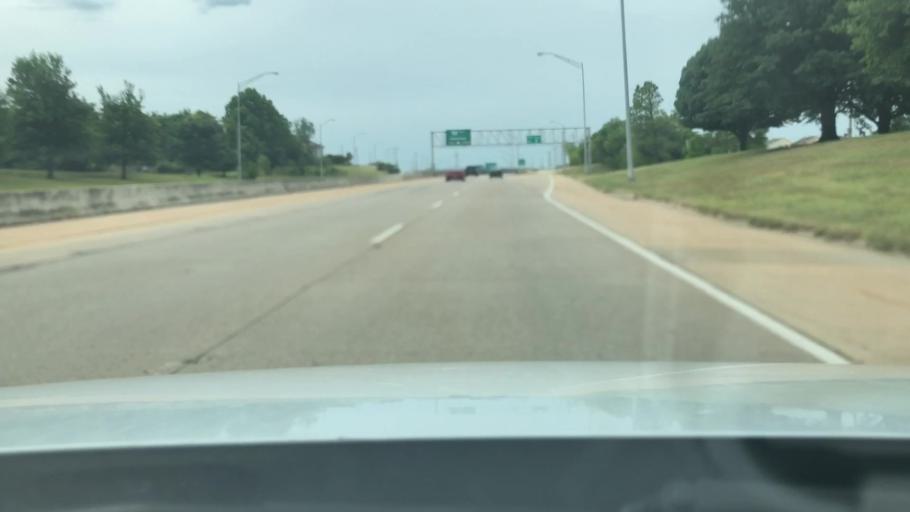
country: US
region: Oklahoma
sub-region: Tulsa County
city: Tulsa
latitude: 36.1664
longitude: -96.0008
